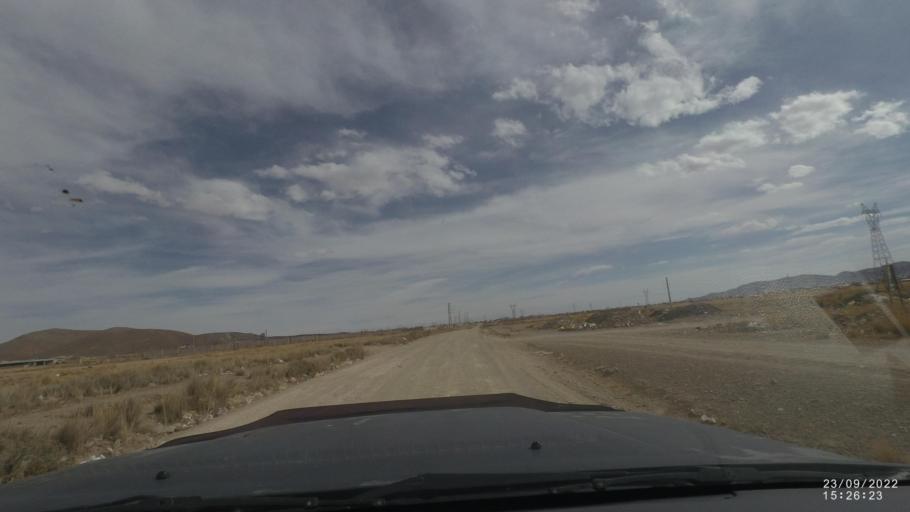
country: BO
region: Oruro
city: Oruro
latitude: -17.9531
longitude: -67.0390
